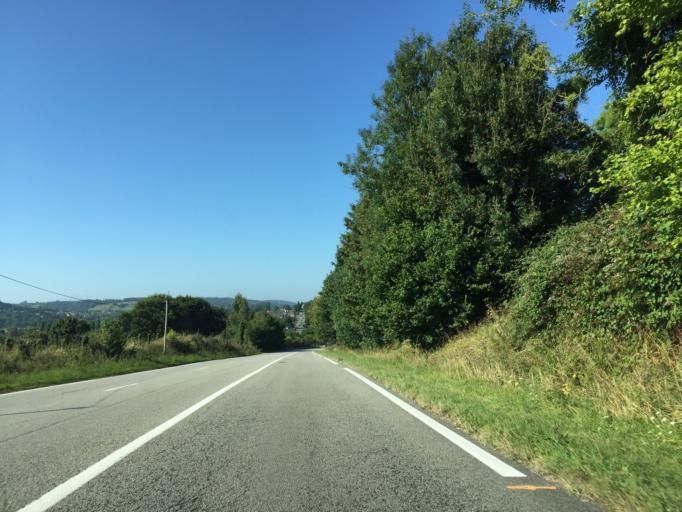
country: FR
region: Lower Normandy
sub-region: Departement du Calvados
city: Lisieux
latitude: 49.1741
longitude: 0.2264
